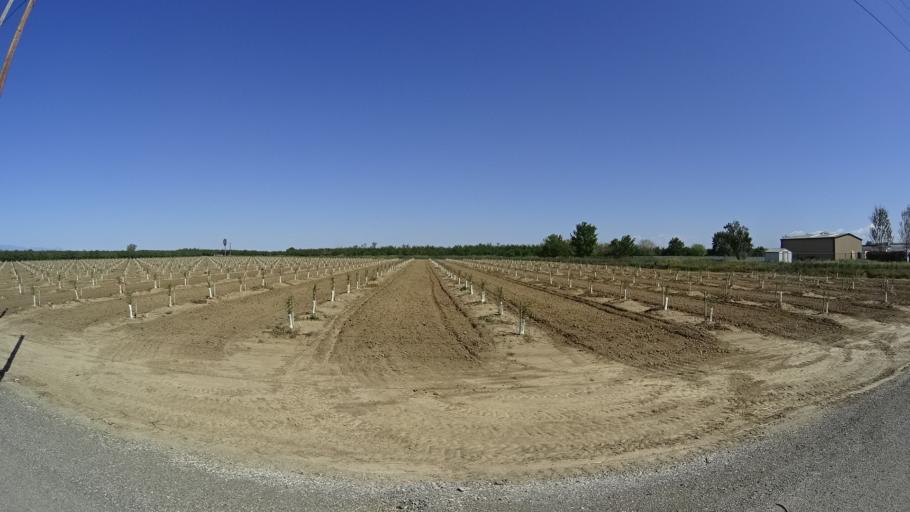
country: US
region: California
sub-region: Glenn County
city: Orland
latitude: 39.7103
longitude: -122.1072
